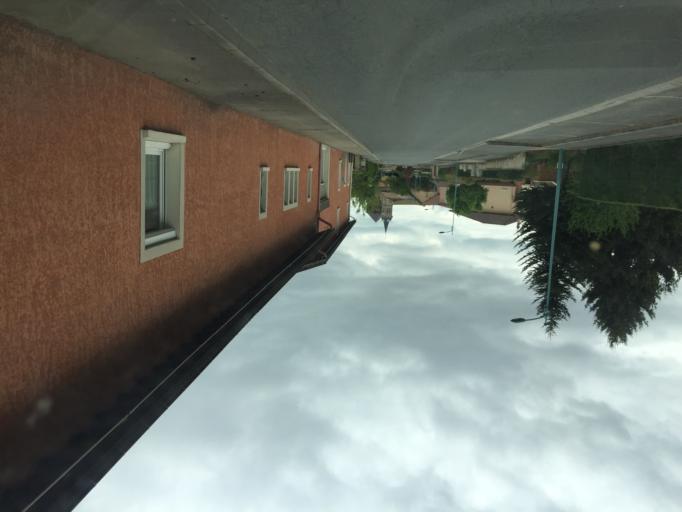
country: FR
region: Rhone-Alpes
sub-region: Departement de l'Ain
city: Amberieux-en-Dombes
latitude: 45.9949
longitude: 4.9057
